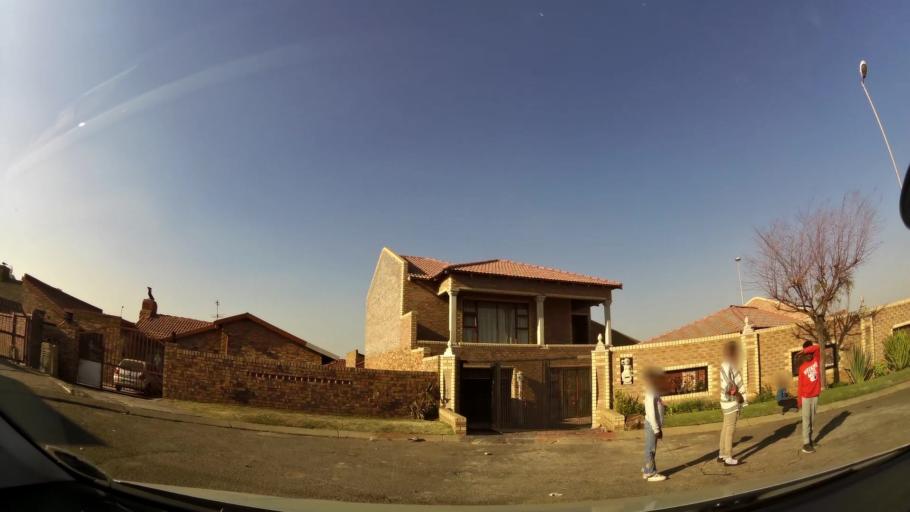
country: ZA
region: Gauteng
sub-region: City of Johannesburg Metropolitan Municipality
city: Soweto
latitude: -26.2670
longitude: 27.8795
